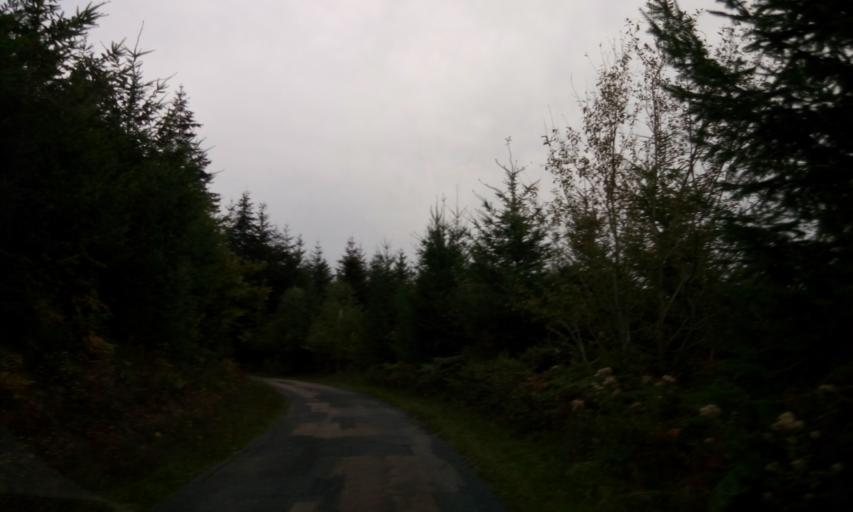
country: FR
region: Rhone-Alpes
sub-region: Departement du Rhone
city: Cublize
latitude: 46.0005
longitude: 4.4154
